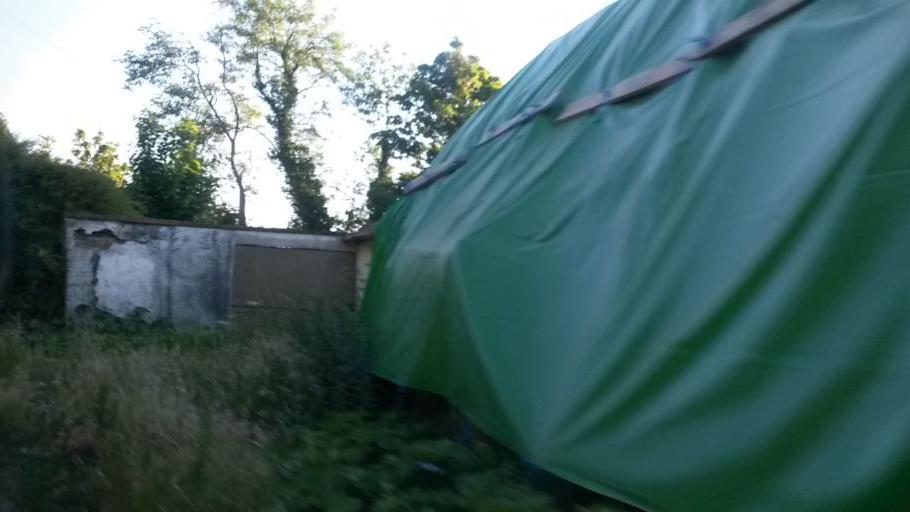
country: IE
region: Leinster
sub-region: An Mhi
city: Ashbourne
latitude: 53.5610
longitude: -6.3846
